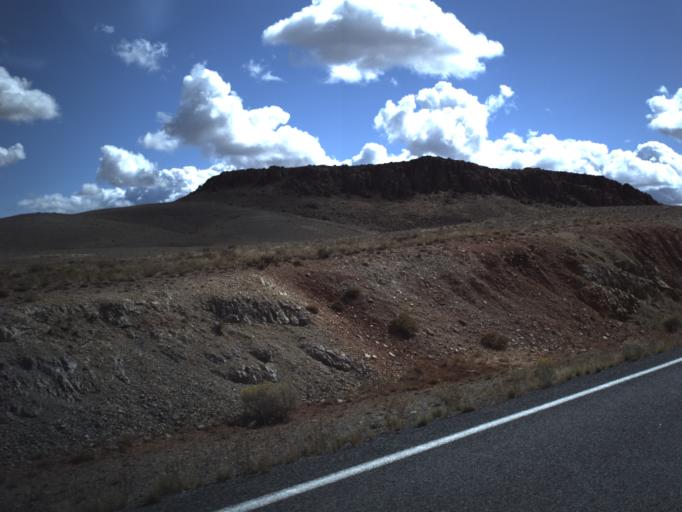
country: US
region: Utah
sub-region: Beaver County
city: Milford
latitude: 38.6215
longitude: -113.8475
